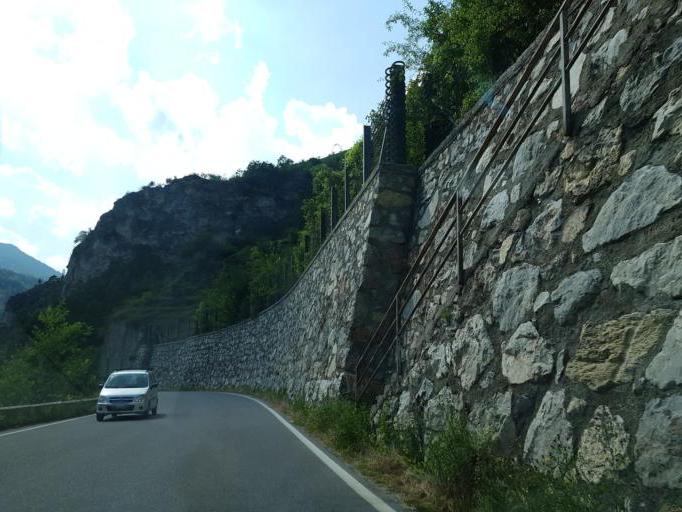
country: IT
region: Piedmont
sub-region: Provincia di Cuneo
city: Macra
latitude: 44.5004
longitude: 7.1764
